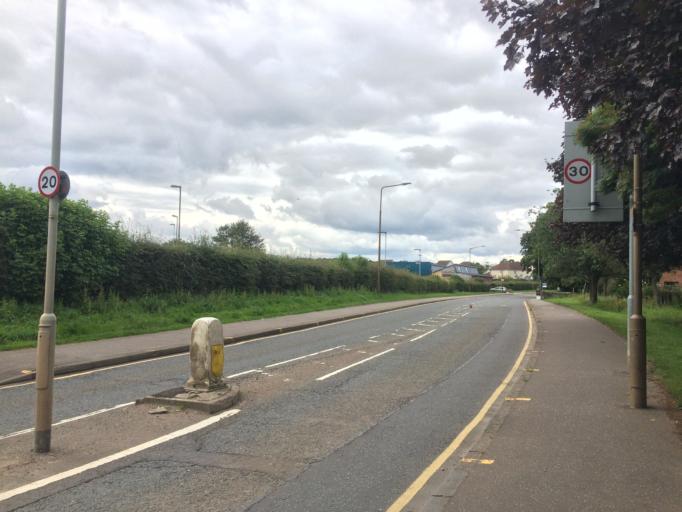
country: GB
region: Scotland
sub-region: Edinburgh
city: Kirkliston
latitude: 55.9568
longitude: -3.4085
